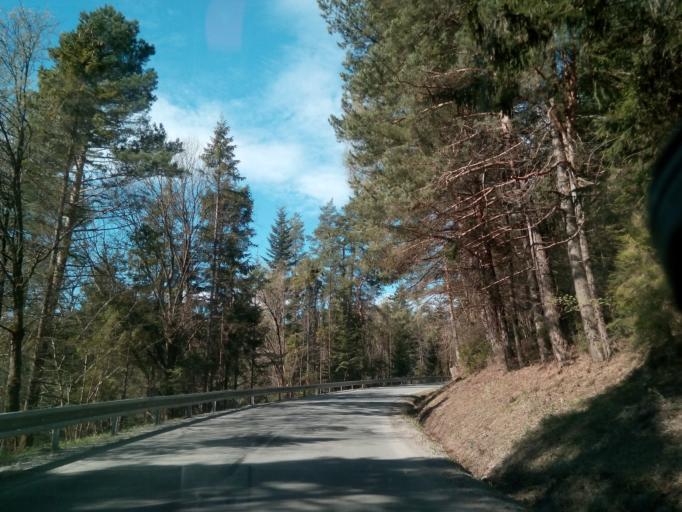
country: PL
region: Lesser Poland Voivodeship
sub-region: Powiat nowotarski
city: Niedzica
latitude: 49.3338
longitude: 20.3219
